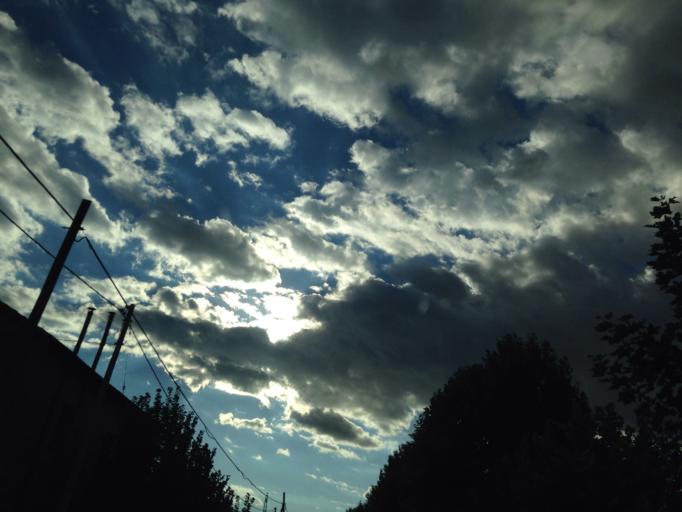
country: IT
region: Friuli Venezia Giulia
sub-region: Provincia di Pordenone
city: Vigonovo-Fontanafredda
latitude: 45.9549
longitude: 12.5422
